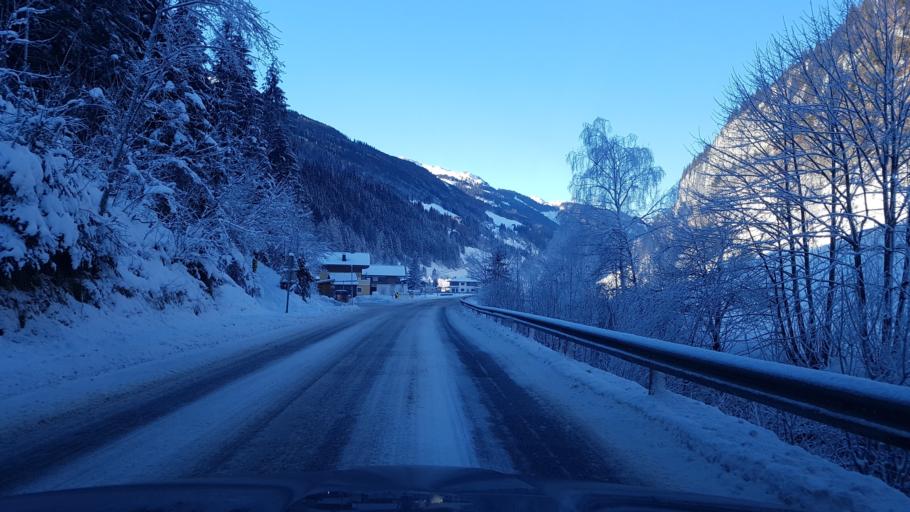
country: AT
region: Salzburg
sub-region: Politischer Bezirk Sankt Johann im Pongau
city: Huttschlag
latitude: 47.1684
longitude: 13.2534
